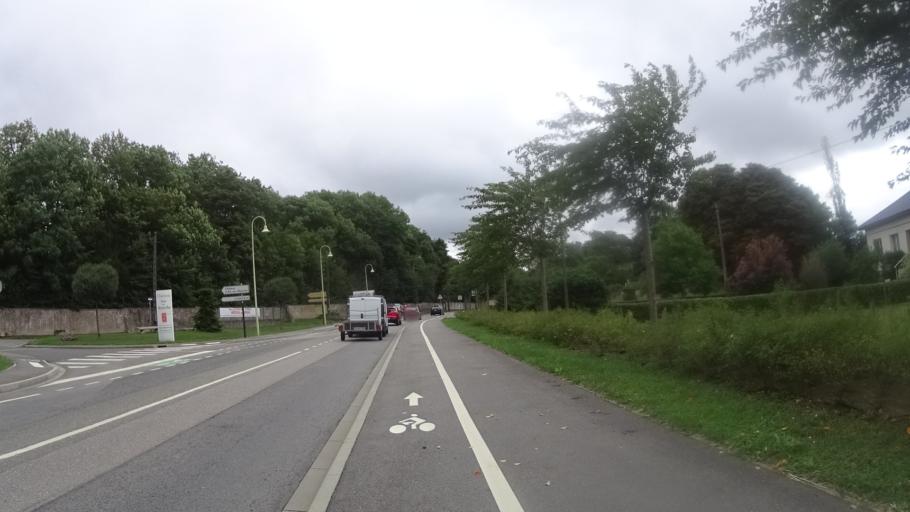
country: FR
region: Lorraine
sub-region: Departement de Meurthe-et-Moselle
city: Art-sur-Meurthe
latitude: 48.6577
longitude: 6.2623
